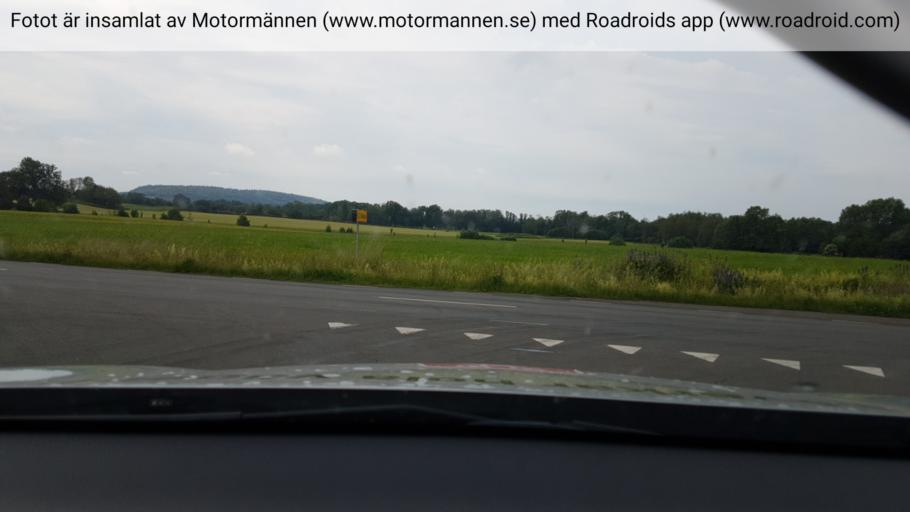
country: SE
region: Vaestra Goetaland
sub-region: Skovde Kommun
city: Skultorp
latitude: 58.3329
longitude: 13.7732
